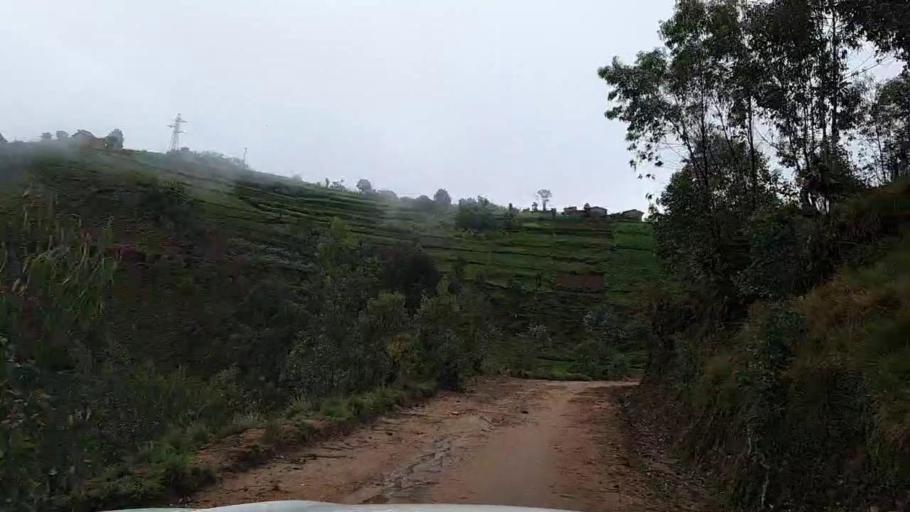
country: RW
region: Southern Province
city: Nzega
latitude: -2.4081
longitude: 29.4918
